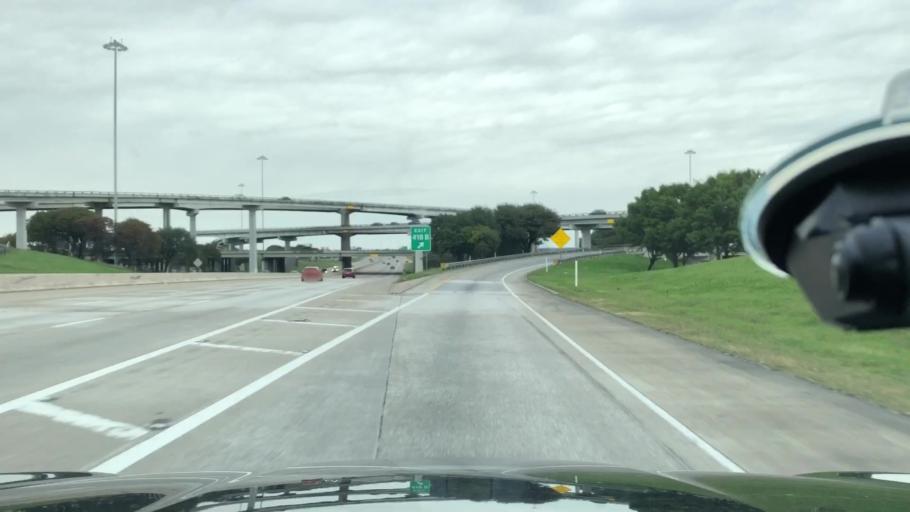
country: US
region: Texas
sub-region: Dallas County
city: DeSoto
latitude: 32.6398
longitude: -96.8230
